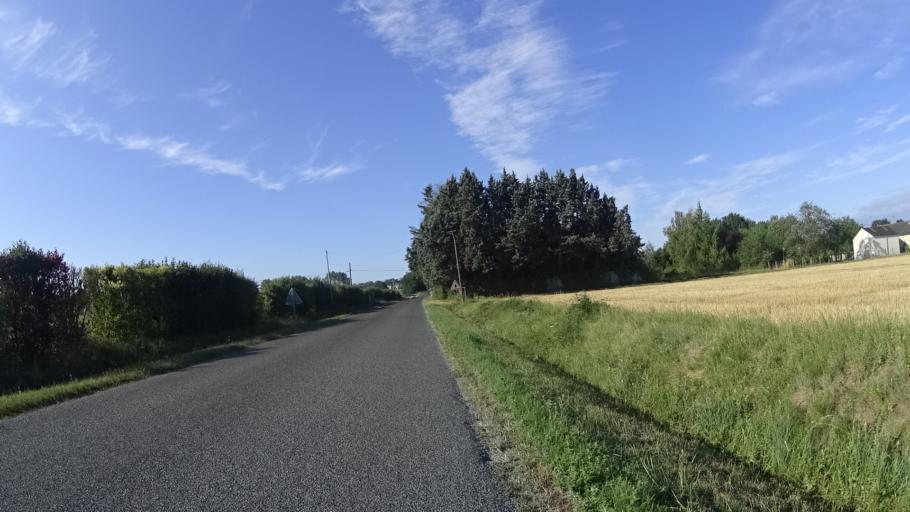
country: FR
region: Pays de la Loire
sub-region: Departement de Maine-et-Loire
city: Varennes-sur-Loire
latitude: 47.2313
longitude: 0.0512
